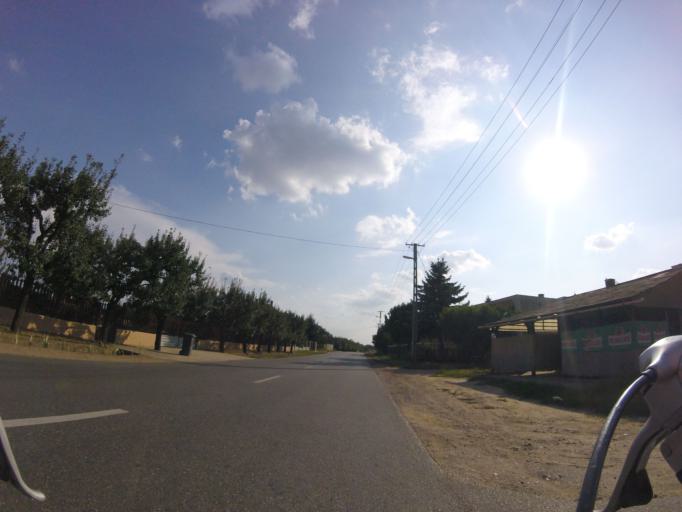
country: HU
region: Szabolcs-Szatmar-Bereg
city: Nyirkarasz
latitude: 48.0931
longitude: 22.0965
